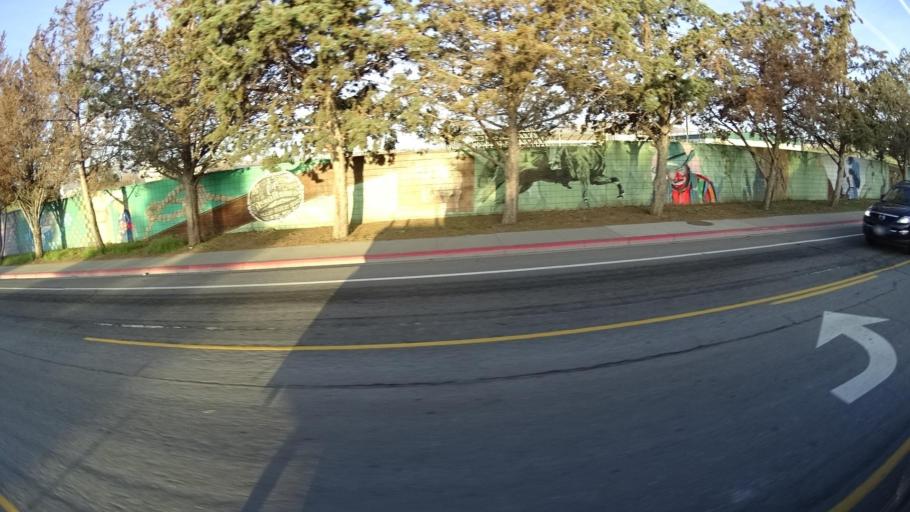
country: US
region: Nevada
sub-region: Washoe County
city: Reno
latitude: 39.5406
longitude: -119.7986
